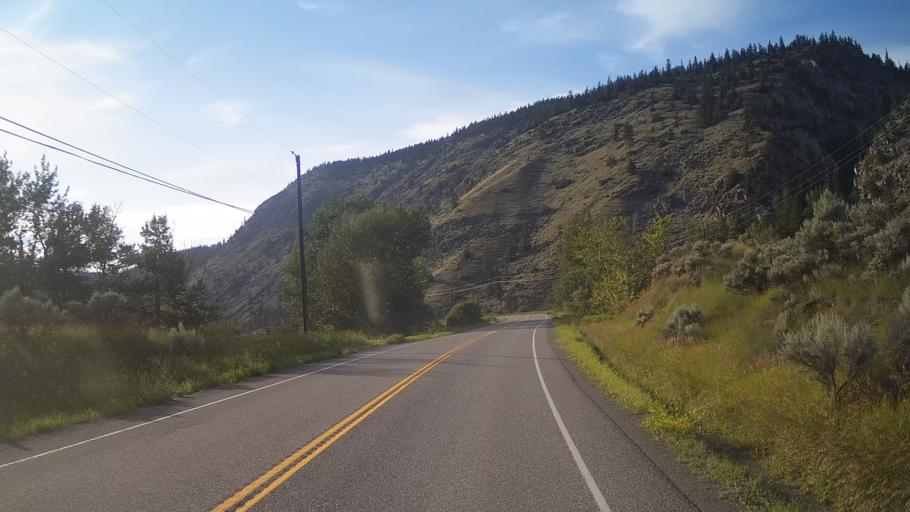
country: CA
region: British Columbia
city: Lillooet
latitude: 50.8910
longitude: -121.7599
